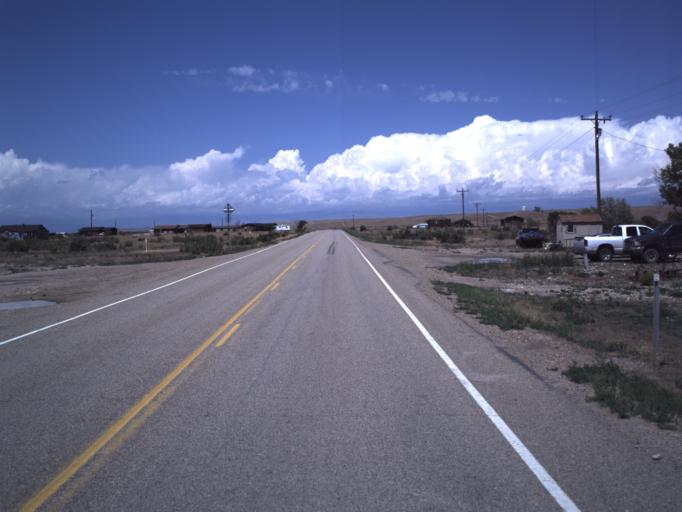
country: US
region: Utah
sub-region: Duchesne County
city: Roosevelt
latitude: 40.0883
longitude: -109.6768
